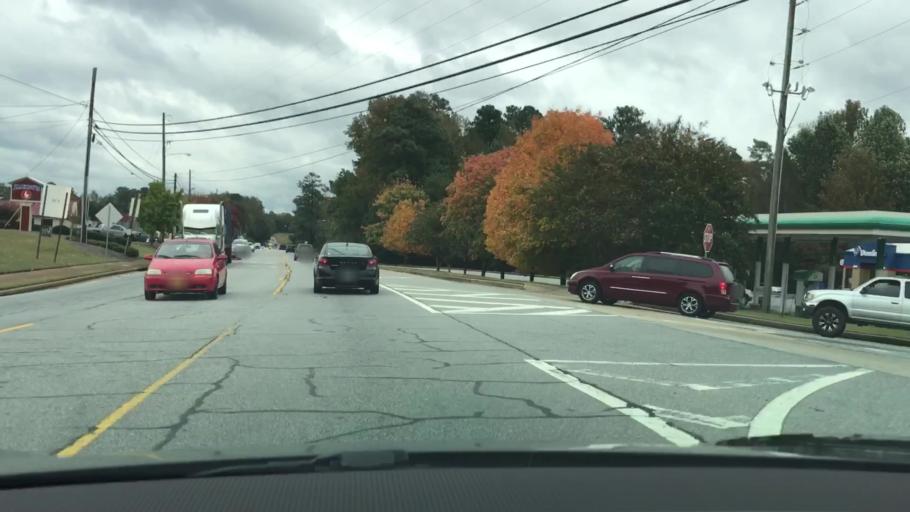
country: US
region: Georgia
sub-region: Oconee County
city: Watkinsville
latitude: 33.8727
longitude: -83.4398
